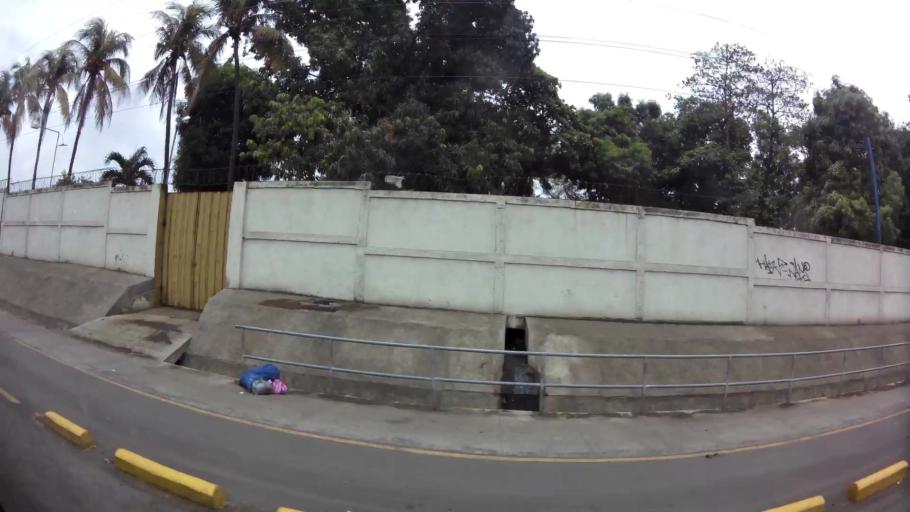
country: NI
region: Leon
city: Leon
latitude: 12.4474
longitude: -86.8634
